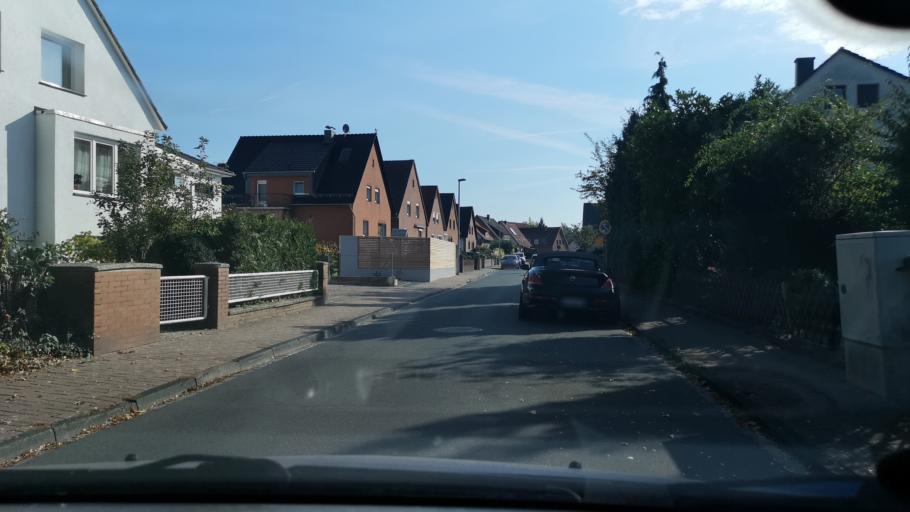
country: DE
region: Lower Saxony
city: Auf der Horst
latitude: 52.4158
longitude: 9.6028
